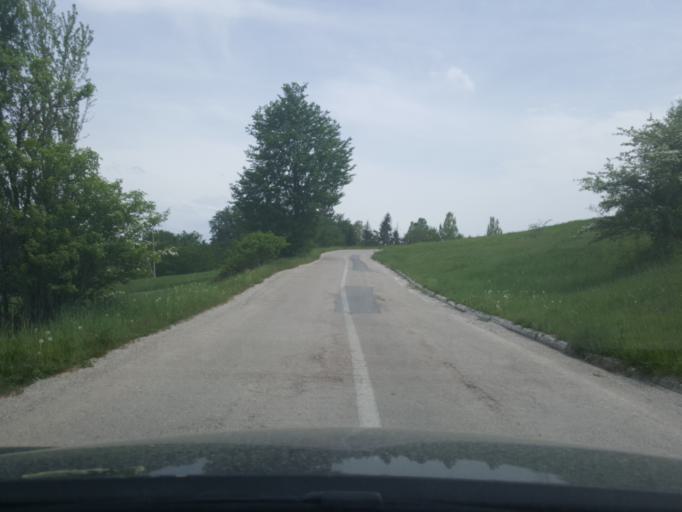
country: RS
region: Central Serbia
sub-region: Zlatiborski Okrug
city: Bajina Basta
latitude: 43.8972
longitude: 19.5200
